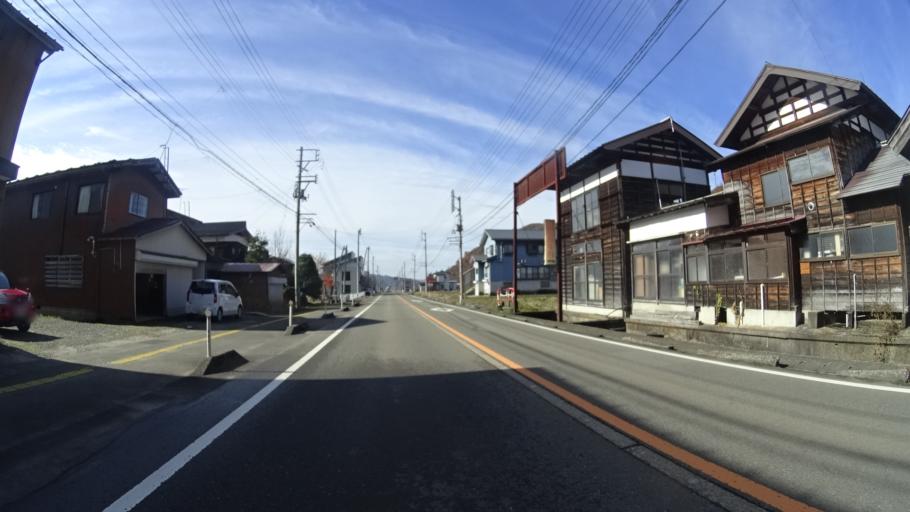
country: JP
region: Niigata
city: Muikamachi
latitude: 37.2270
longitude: 139.0008
